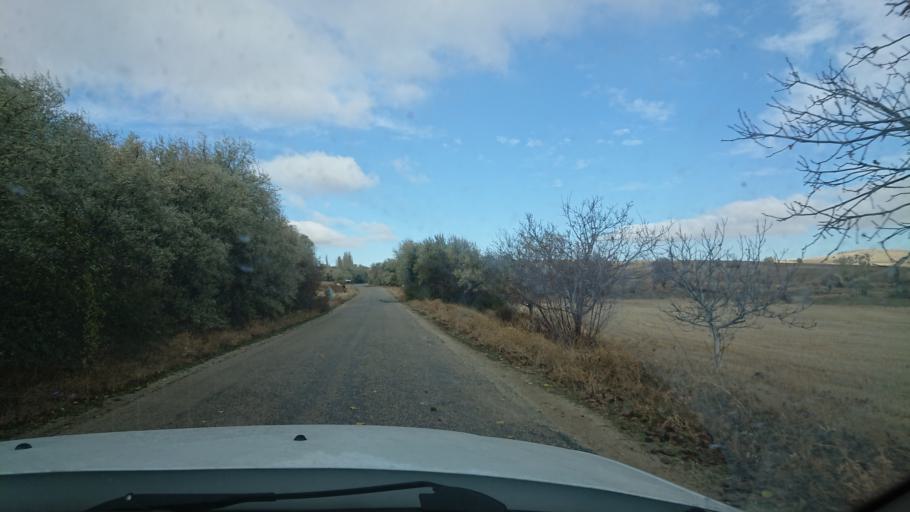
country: TR
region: Aksaray
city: Agacoren
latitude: 38.8282
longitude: 33.9573
